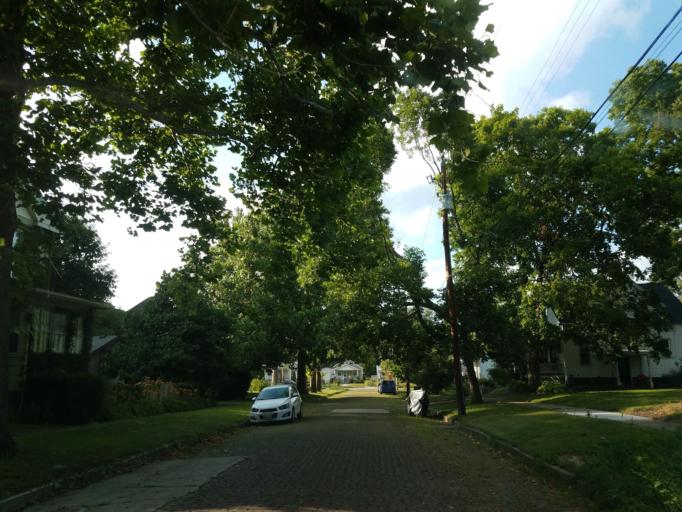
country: US
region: Illinois
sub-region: McLean County
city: Bloomington
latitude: 40.4892
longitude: -88.9874
